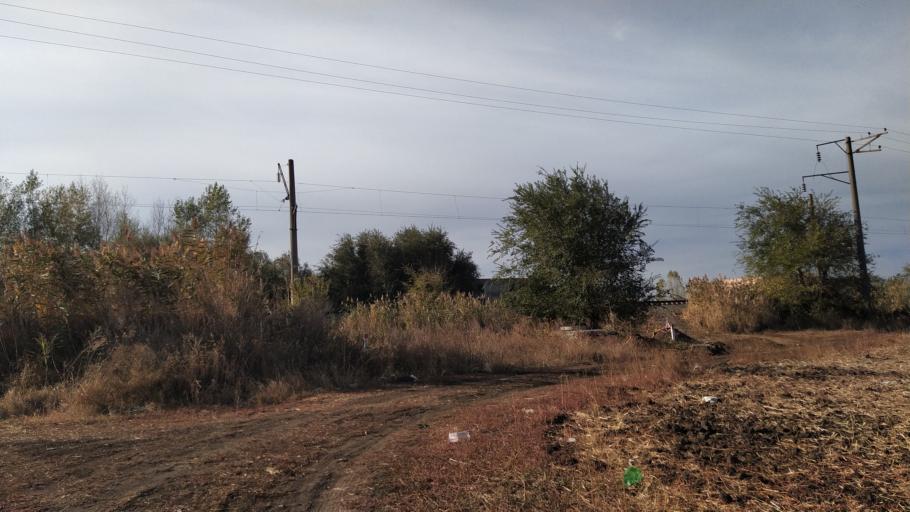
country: RU
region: Rostov
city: Bataysk
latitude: 47.1140
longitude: 39.7141
